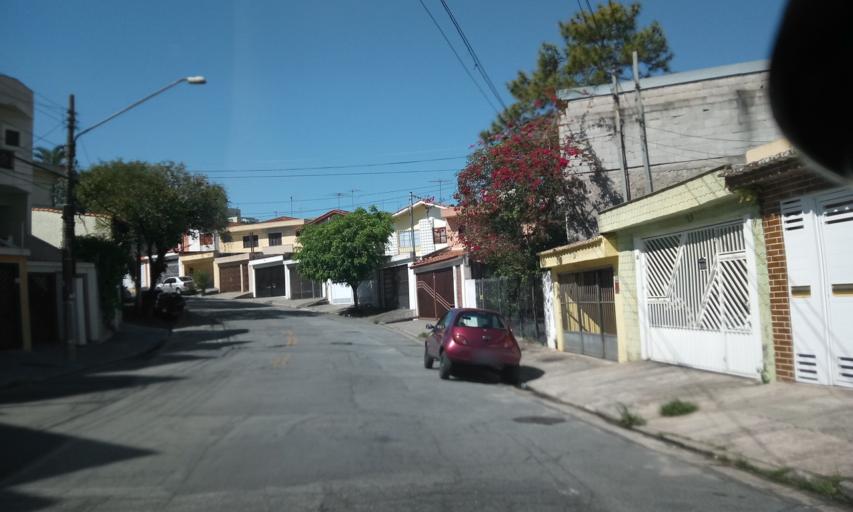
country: BR
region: Sao Paulo
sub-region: Sao Bernardo Do Campo
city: Sao Bernardo do Campo
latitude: -23.7220
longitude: -46.5709
